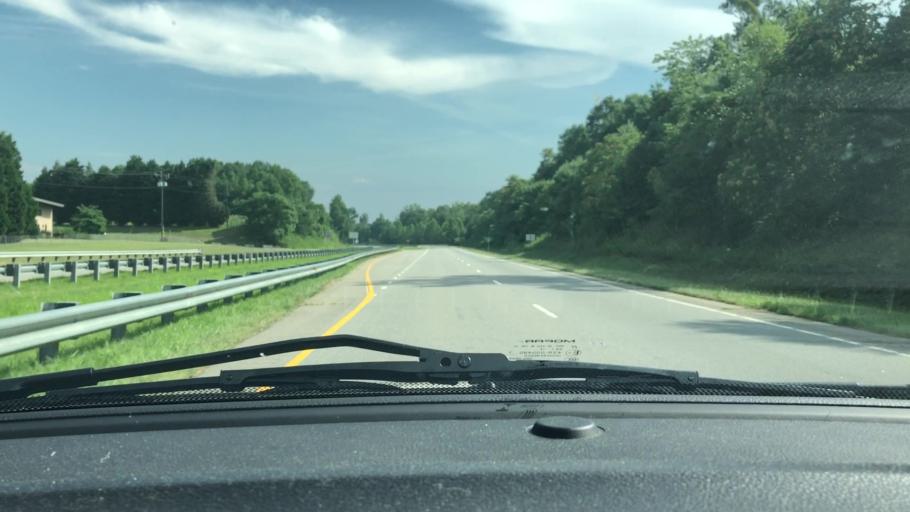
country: US
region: North Carolina
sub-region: Rockingham County
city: Stoneville
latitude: 36.4941
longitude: -79.9240
